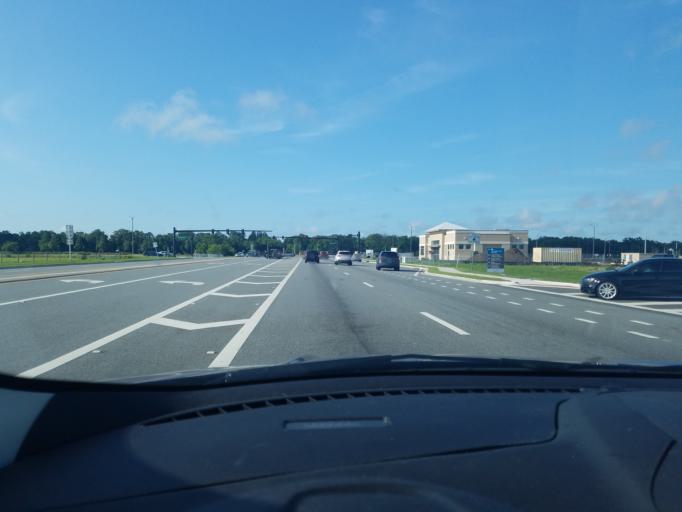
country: US
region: Florida
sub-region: Osceola County
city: Buenaventura Lakes
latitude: 28.3665
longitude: -81.3097
